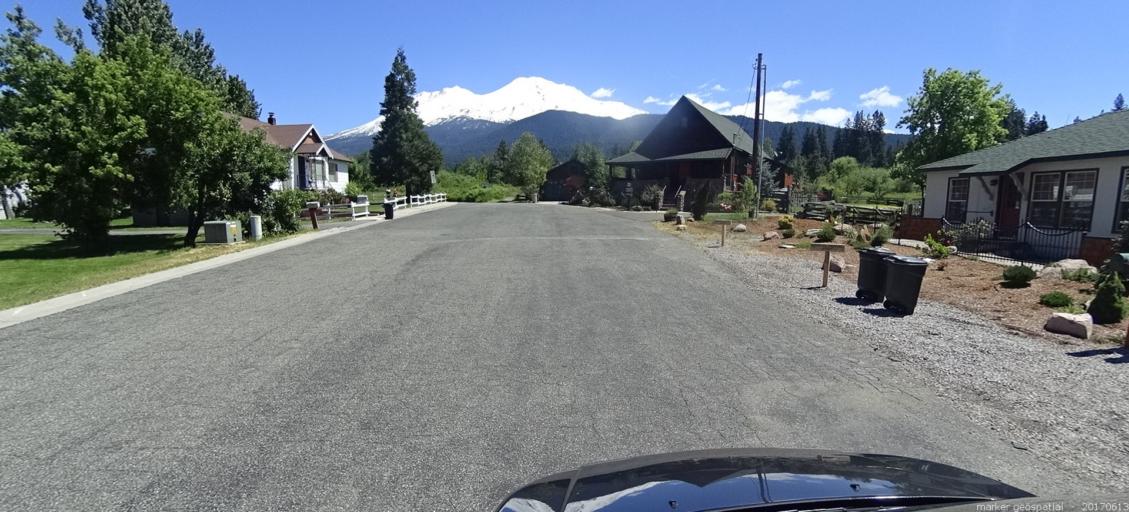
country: US
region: California
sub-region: Siskiyou County
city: Mount Shasta
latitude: 41.3156
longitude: -122.3116
